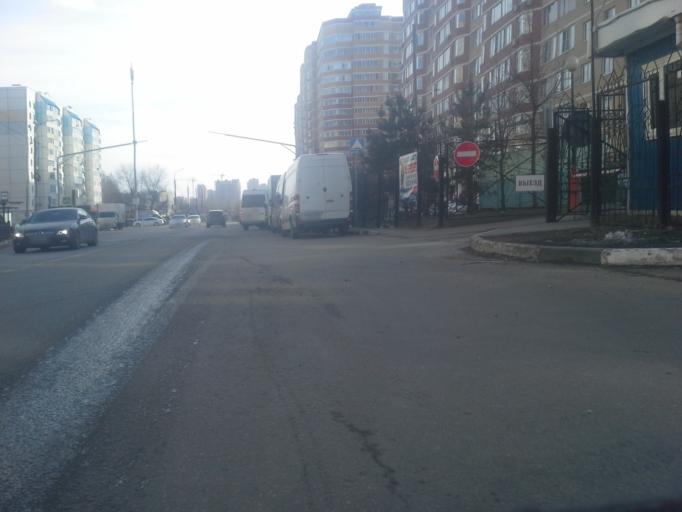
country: RU
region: Moskovskaya
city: Shcherbinka
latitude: 55.4693
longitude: 37.5455
